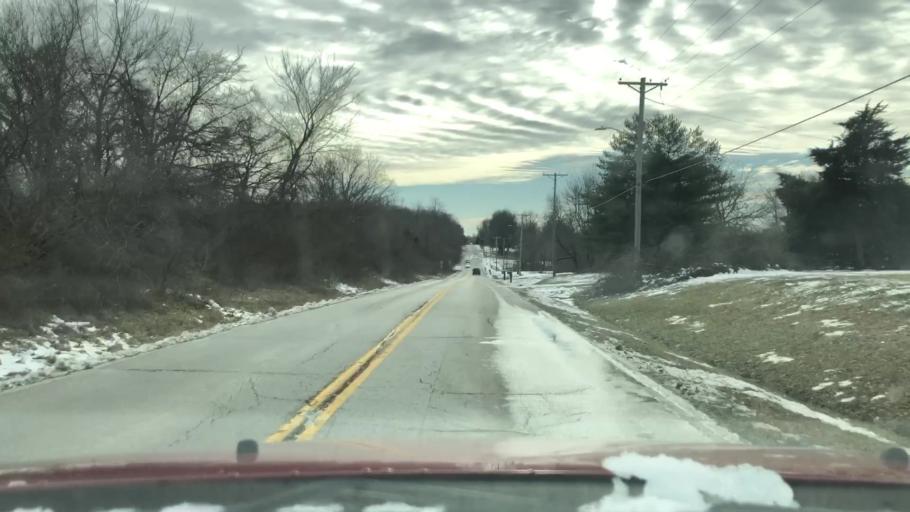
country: US
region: Missouri
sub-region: Jackson County
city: Greenwood
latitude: 38.8703
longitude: -94.3416
